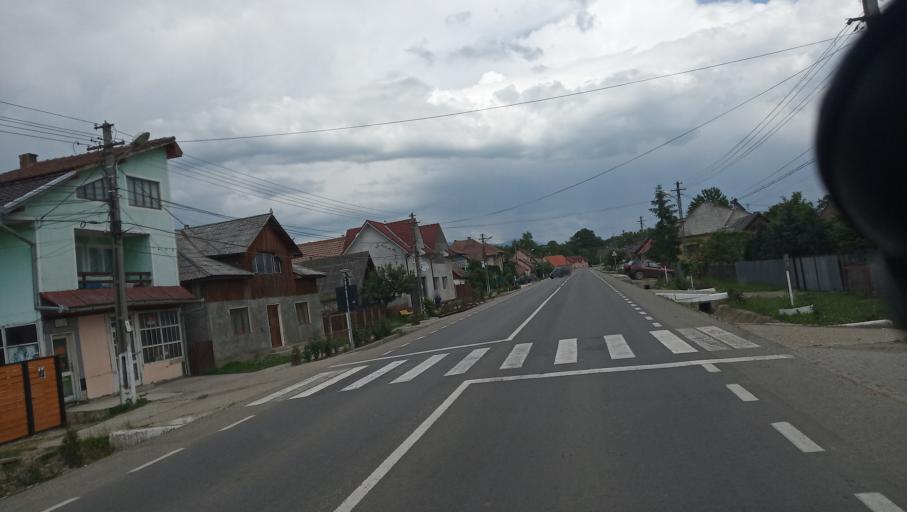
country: RO
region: Bistrita-Nasaud
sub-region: Comuna Livezile
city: Livezile
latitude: 47.1817
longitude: 24.5620
